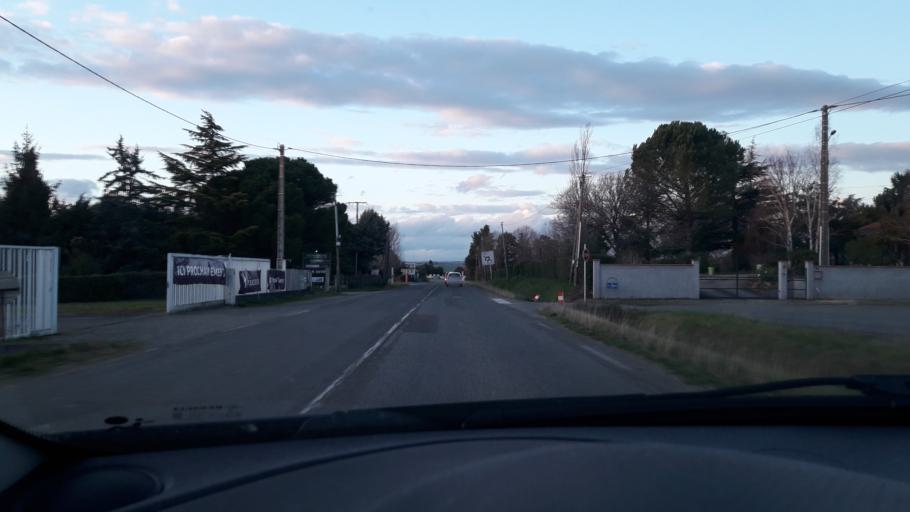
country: FR
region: Midi-Pyrenees
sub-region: Departement du Gers
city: Pujaudran
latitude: 43.6070
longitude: 1.1004
